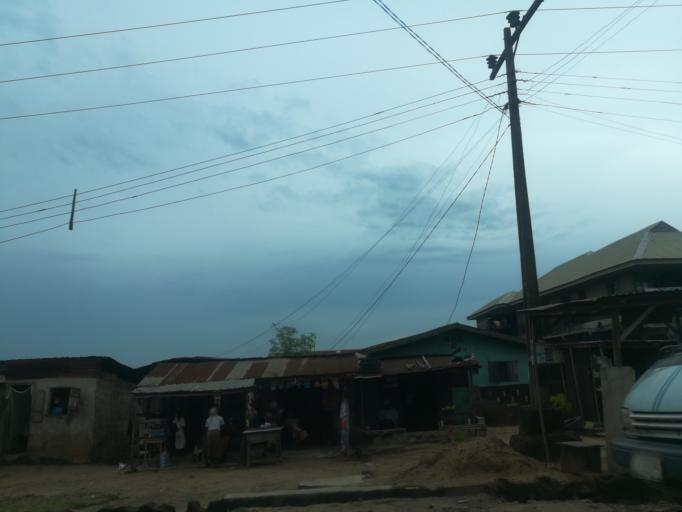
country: NG
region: Oyo
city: Egbeda
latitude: 7.3854
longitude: 3.9937
